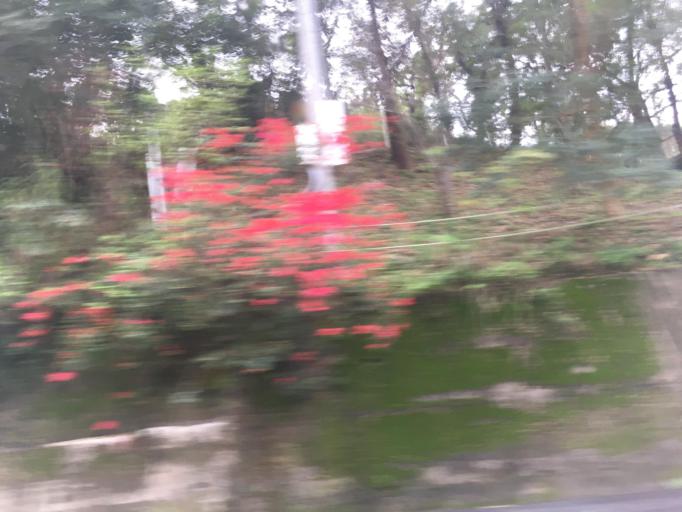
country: TW
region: Taiwan
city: Fengyuan
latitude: 24.4121
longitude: 120.7352
